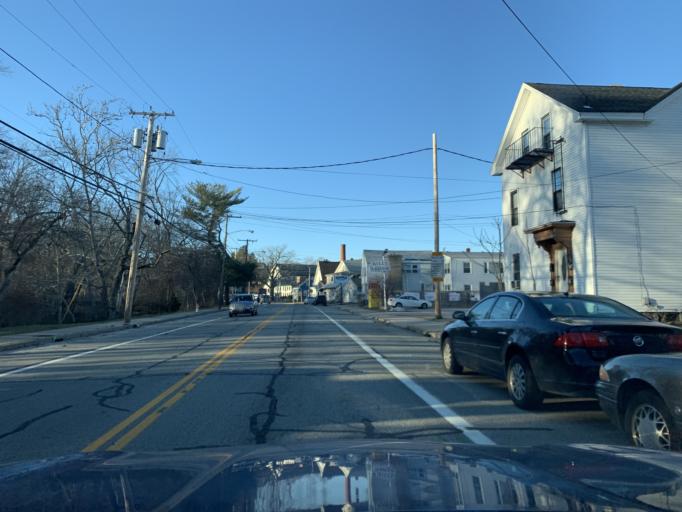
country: US
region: Rhode Island
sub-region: Kent County
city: West Warwick
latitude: 41.7232
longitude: -71.5345
